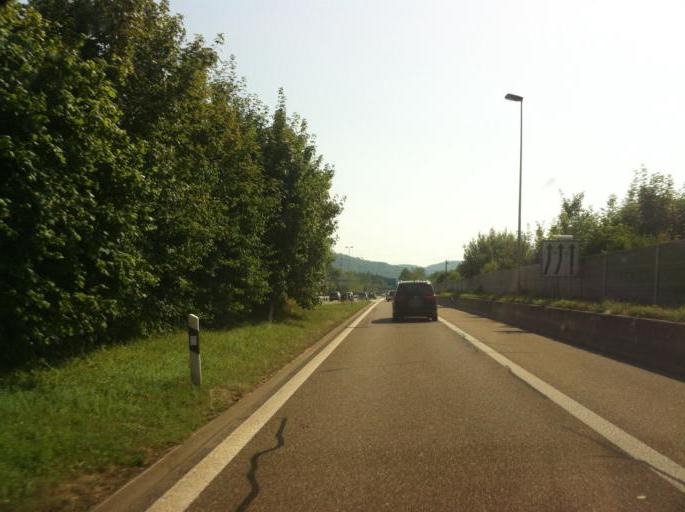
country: CH
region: Zurich
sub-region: Bezirk Winterthur
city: Wuelflingen (Kreis 6) / Lindenplatz
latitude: 47.5232
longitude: 8.6999
